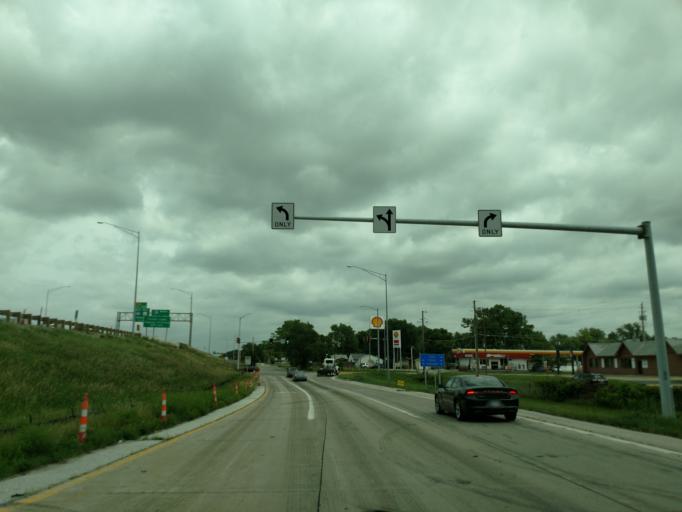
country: US
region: Nebraska
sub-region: Douglas County
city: Omaha
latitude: 41.2527
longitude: -95.9064
